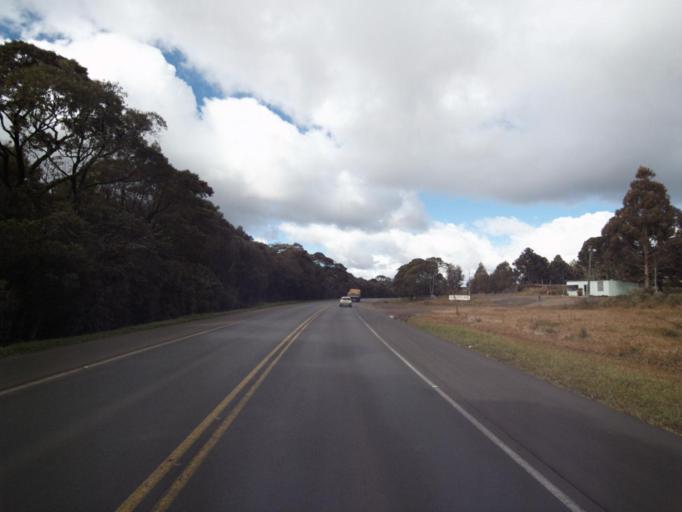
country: BR
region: Santa Catarina
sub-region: Concordia
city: Concordia
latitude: -26.9723
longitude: -51.8328
